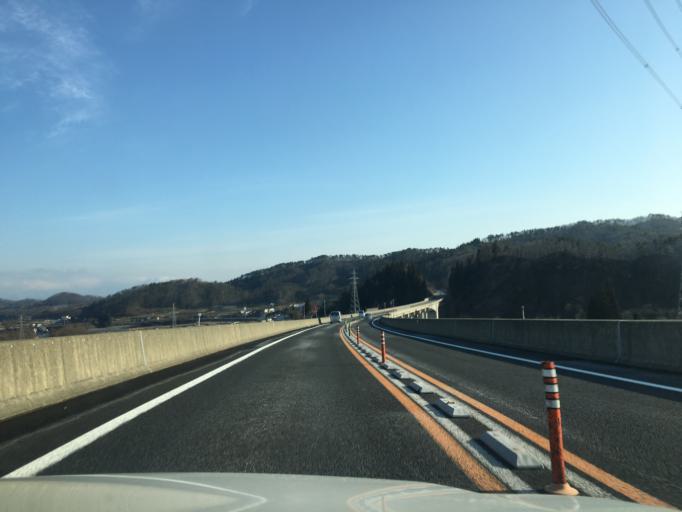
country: JP
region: Yamagata
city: Sagae
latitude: 38.4151
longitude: 140.1893
